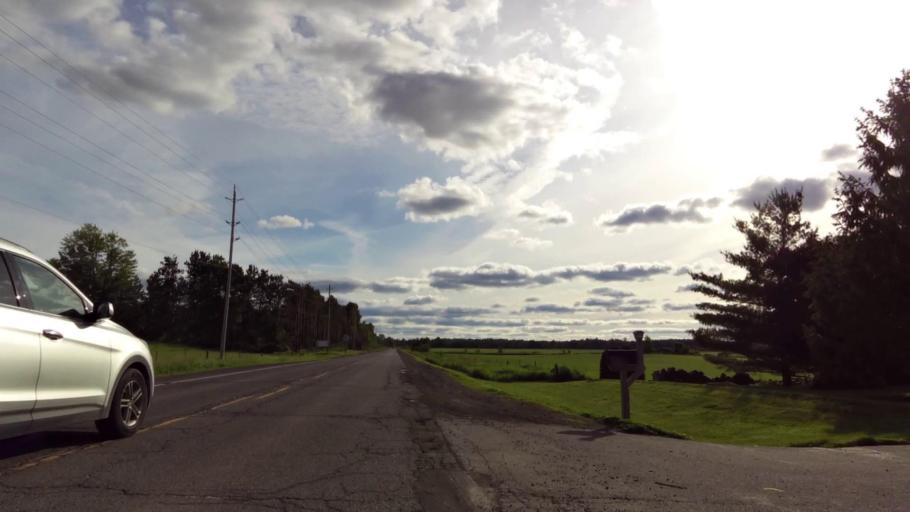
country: CA
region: Ontario
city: Ottawa
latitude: 45.1944
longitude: -75.5702
